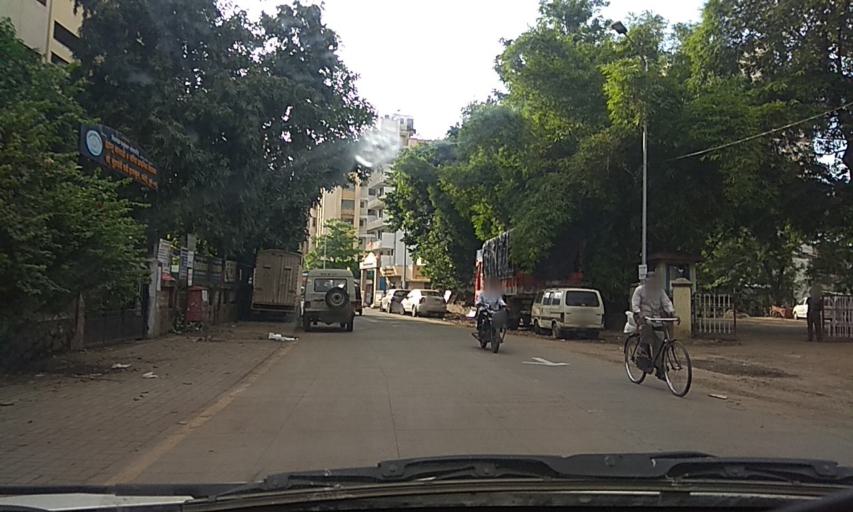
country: IN
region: Maharashtra
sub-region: Pune Division
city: Pune
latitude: 18.4974
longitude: 73.8529
